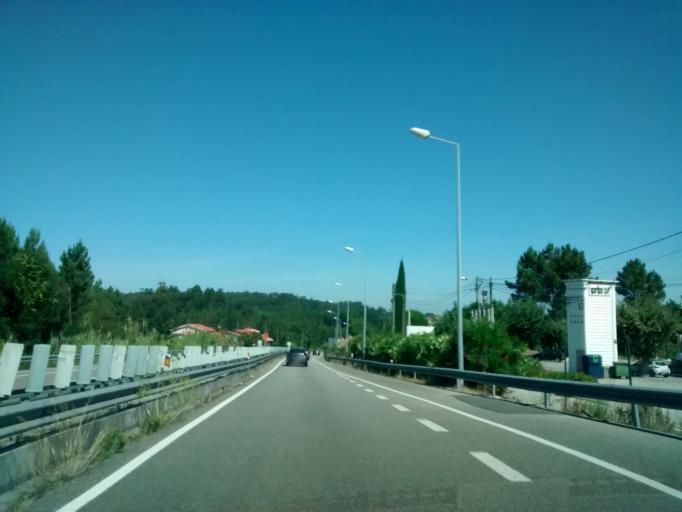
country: PT
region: Aveiro
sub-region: Oliveira do Bairro
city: Oliveira do Bairro
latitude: 40.5251
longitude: -8.5067
